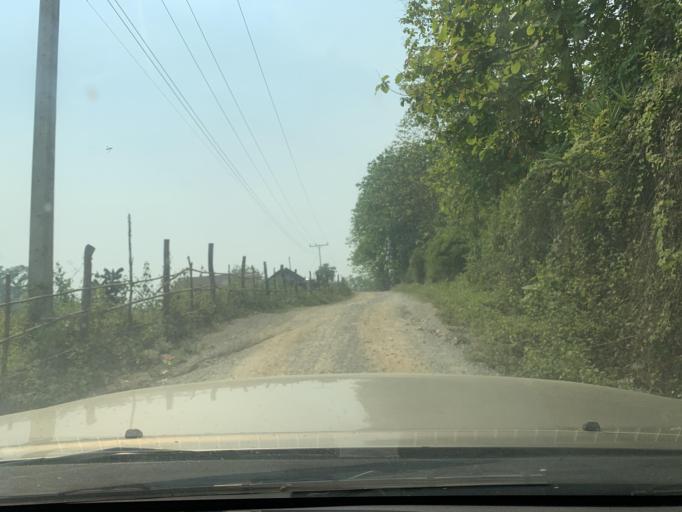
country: LA
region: Louangphabang
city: Louangphabang
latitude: 19.8834
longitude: 102.2567
